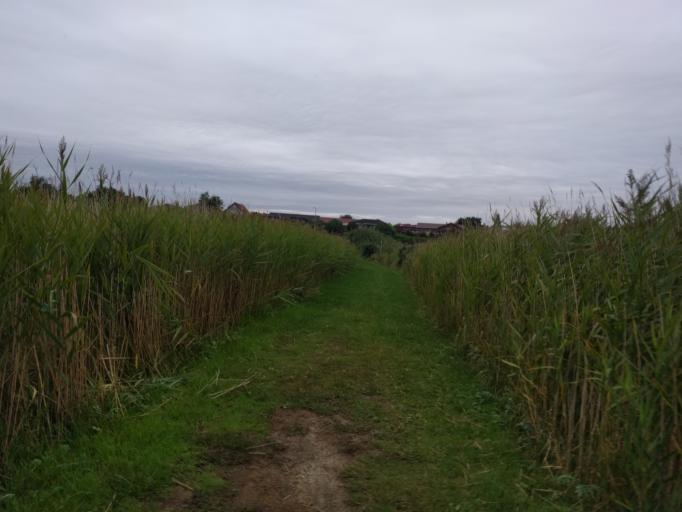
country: DK
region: South Denmark
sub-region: Kerteminde Kommune
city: Munkebo
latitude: 55.4449
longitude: 10.5427
